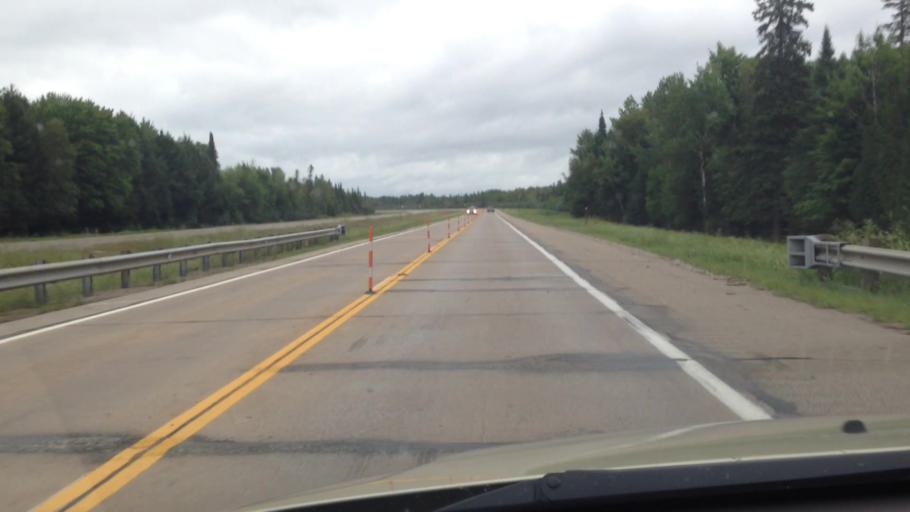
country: US
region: Michigan
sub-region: Delta County
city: Gladstone
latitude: 45.8959
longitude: -86.9977
